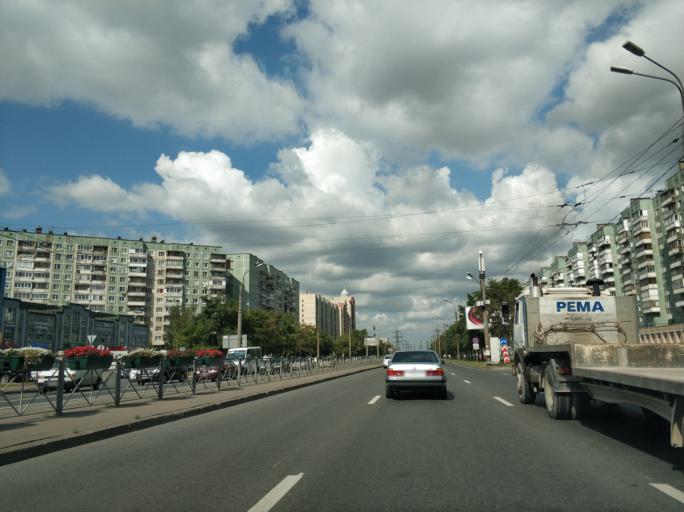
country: RU
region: St.-Petersburg
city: Krasnogvargeisky
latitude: 59.9516
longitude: 30.4715
